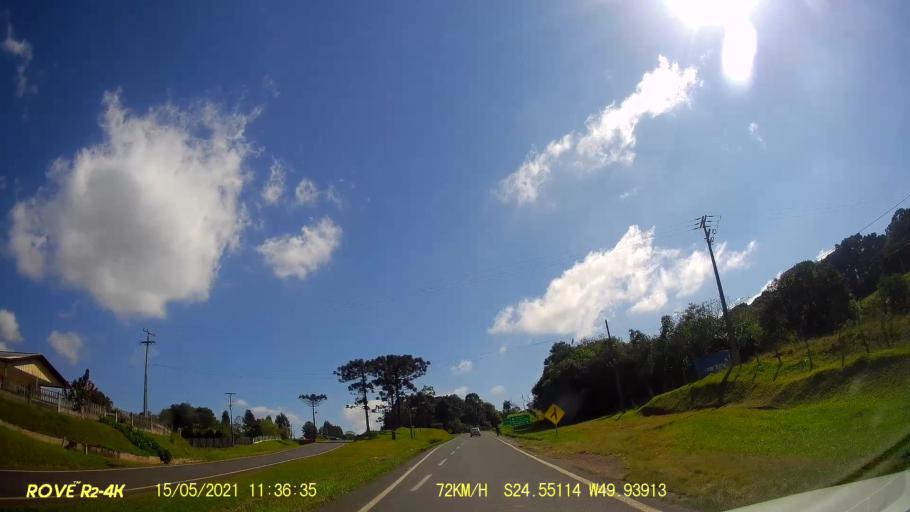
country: BR
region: Parana
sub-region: Pirai Do Sul
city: Pirai do Sul
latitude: -24.5512
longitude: -49.9389
